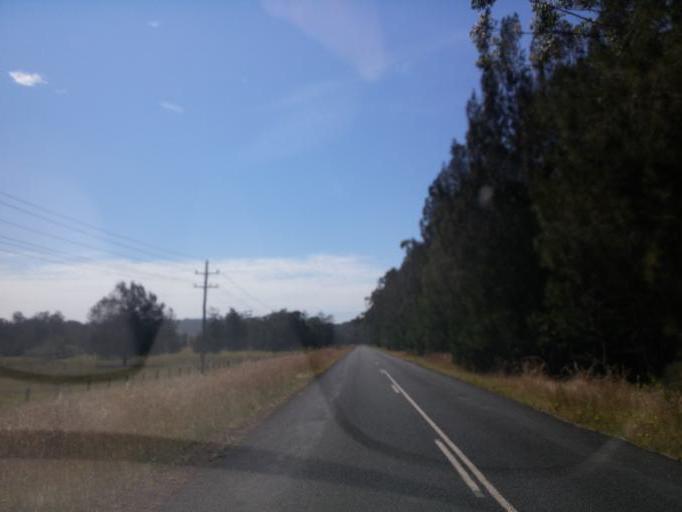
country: AU
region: New South Wales
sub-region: Great Lakes
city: Bulahdelah
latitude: -32.3903
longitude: 152.3300
